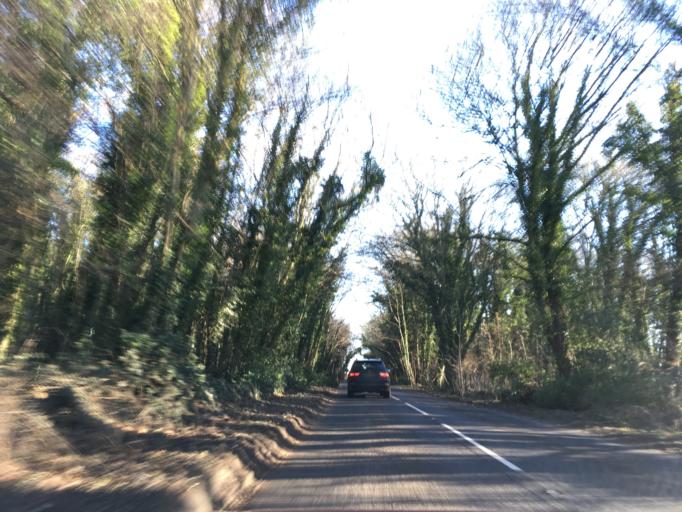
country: GB
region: England
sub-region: Wiltshire
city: Biddestone
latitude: 51.4931
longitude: -2.2077
